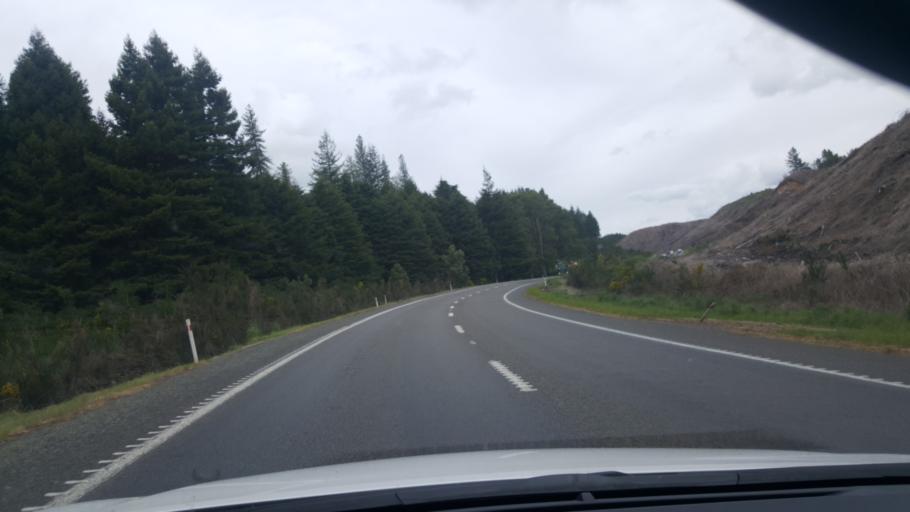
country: NZ
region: Bay of Plenty
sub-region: Rotorua District
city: Rotorua
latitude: -38.2285
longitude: 176.2968
